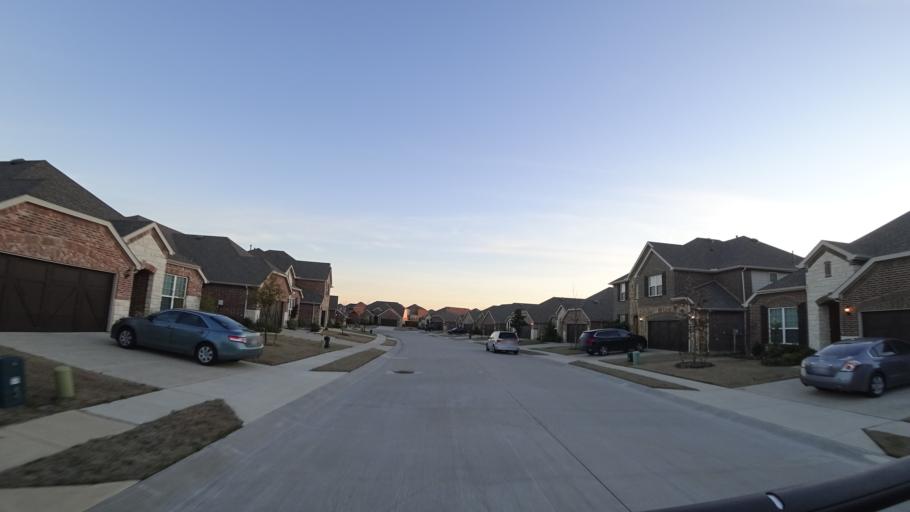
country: US
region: Texas
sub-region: Denton County
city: Lewisville
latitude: 32.9983
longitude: -96.9892
